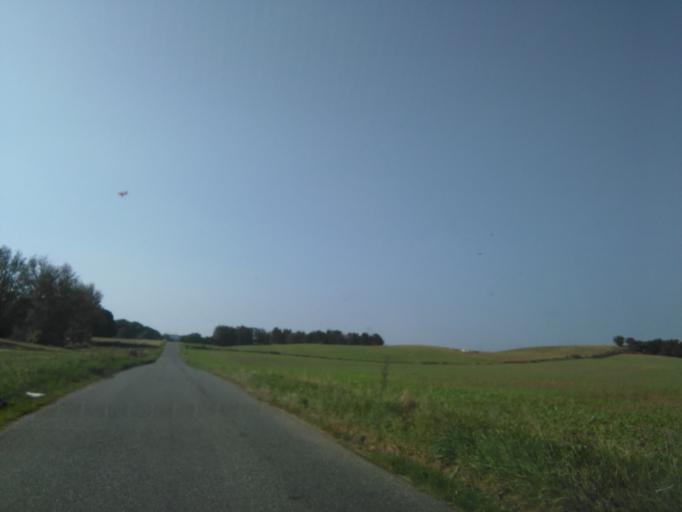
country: DK
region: Central Jutland
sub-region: Syddjurs Kommune
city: Ronde
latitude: 56.1933
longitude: 10.4291
